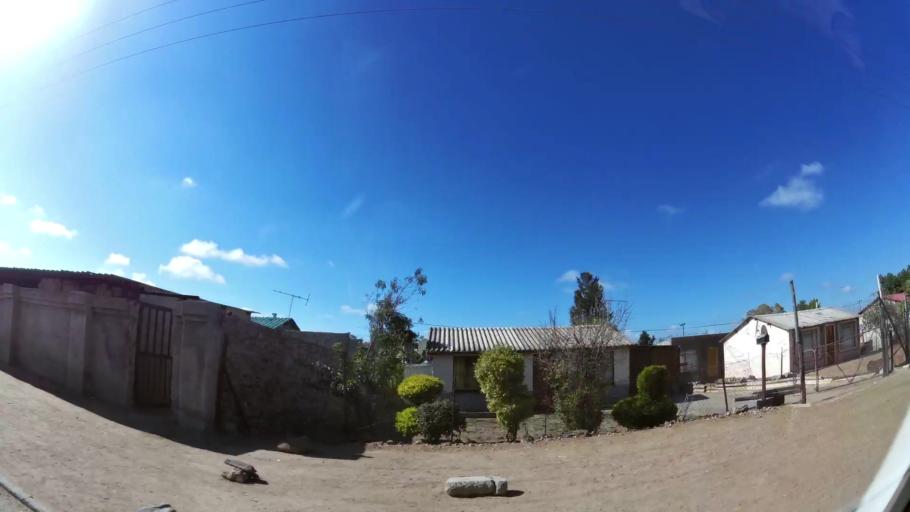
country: ZA
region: Limpopo
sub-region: Capricorn District Municipality
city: Polokwane
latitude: -23.8663
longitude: 29.3895
